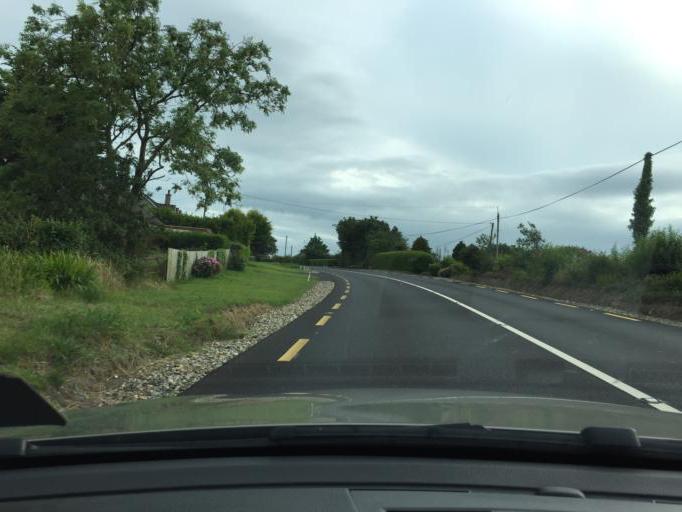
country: IE
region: Leinster
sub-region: Wicklow
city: Arklow
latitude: 52.8275
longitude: -6.1367
